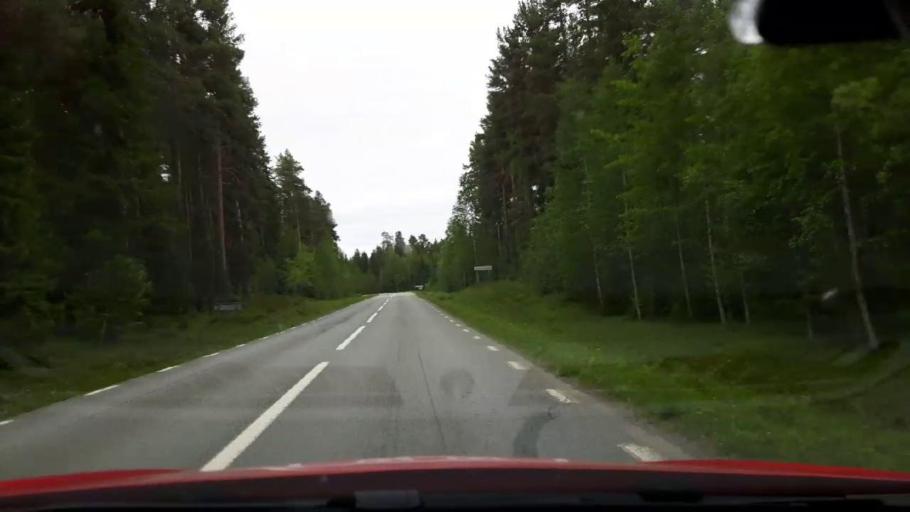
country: SE
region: Jaemtland
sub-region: Stroemsunds Kommun
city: Stroemsund
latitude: 63.3901
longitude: 15.6748
